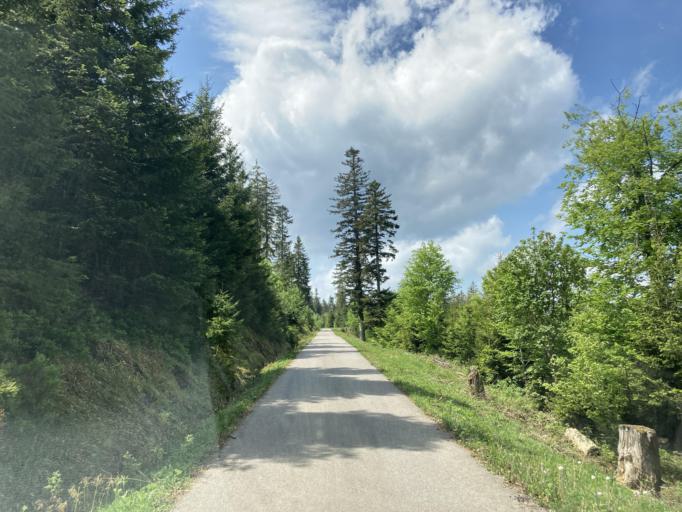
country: DE
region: Baden-Wuerttemberg
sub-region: Freiburg Region
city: Bad Peterstal-Griesbach
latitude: 48.4981
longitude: 8.2577
